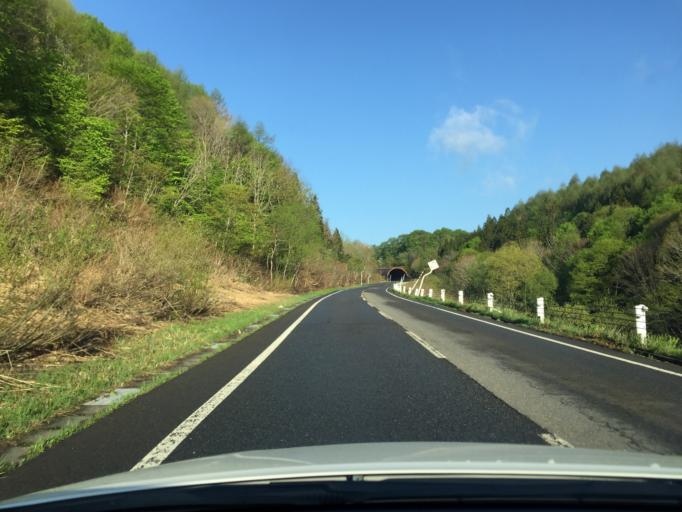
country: JP
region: Fukushima
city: Inawashiro
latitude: 37.6686
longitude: 140.0404
